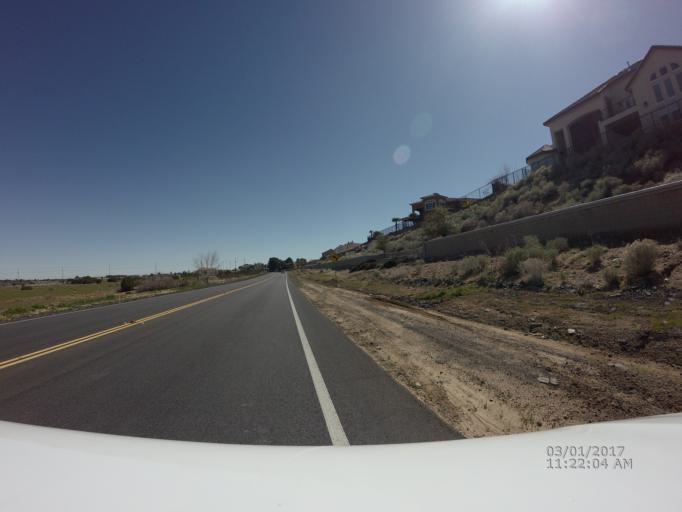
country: US
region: California
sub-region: Los Angeles County
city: Quartz Hill
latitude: 34.6462
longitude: -118.1962
